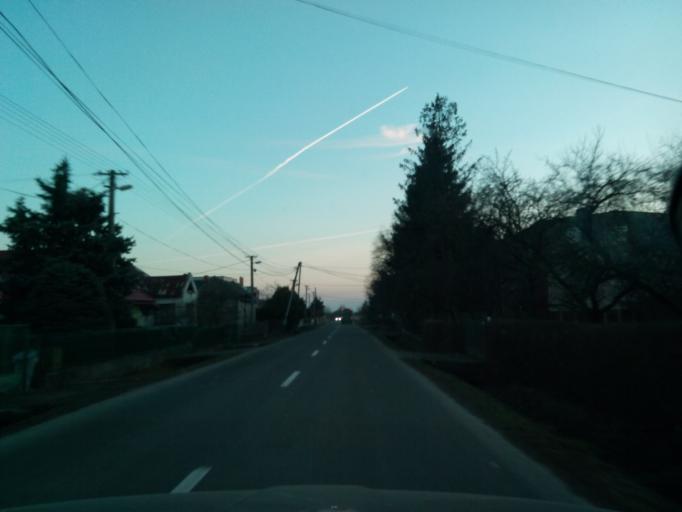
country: SK
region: Kosicky
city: Sobrance
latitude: 48.7854
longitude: 22.1318
